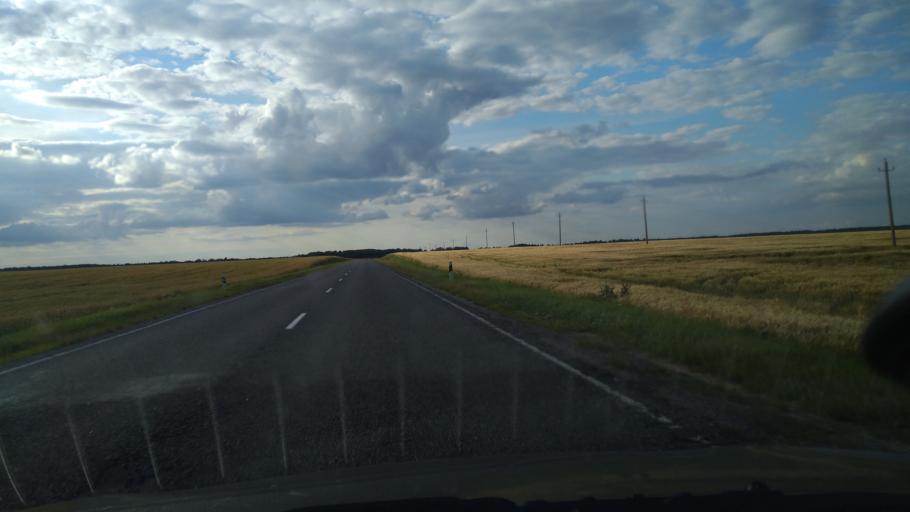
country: BY
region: Grodnenskaya
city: Masty
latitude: 53.3297
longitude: 24.6778
